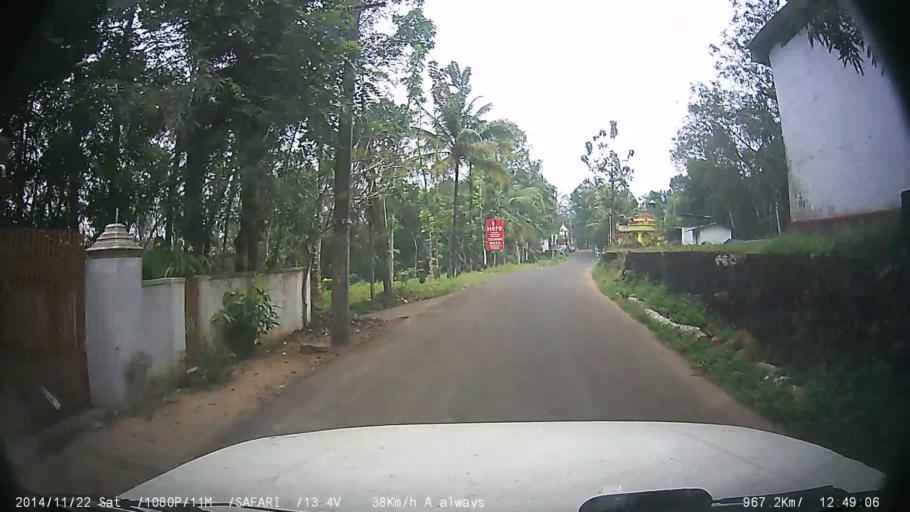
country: IN
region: Kerala
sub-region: Ernakulam
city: Piravam
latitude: 9.7909
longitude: 76.5487
